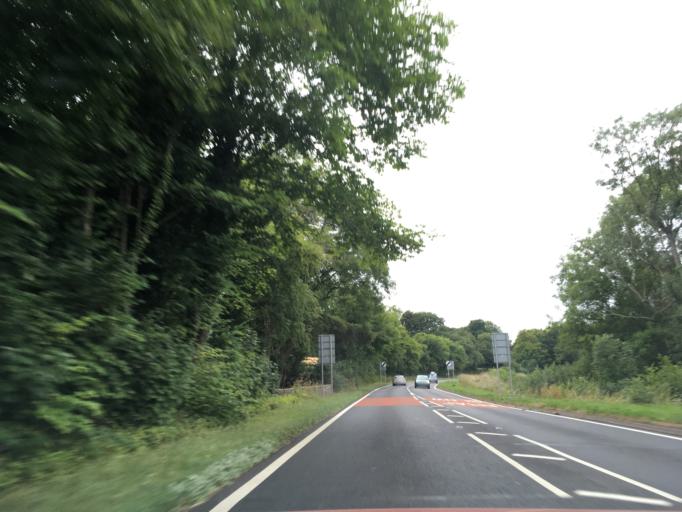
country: GB
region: Wales
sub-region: Sir Powys
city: Brecon
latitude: 51.9440
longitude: -3.4424
